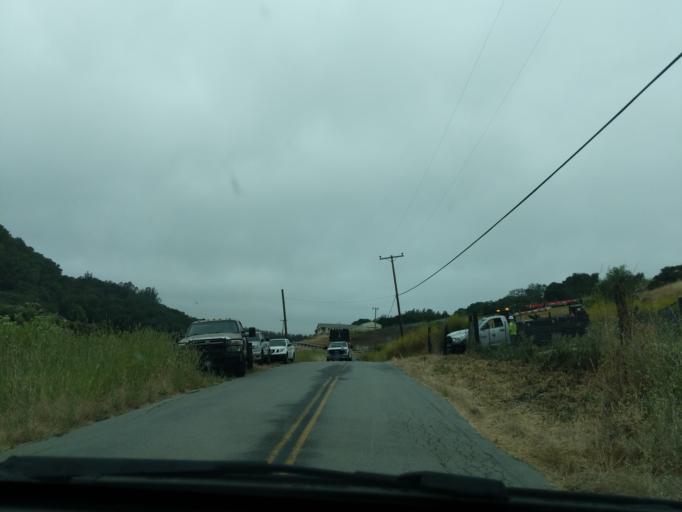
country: US
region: California
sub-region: San Benito County
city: Aromas
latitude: 36.8854
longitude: -121.5908
